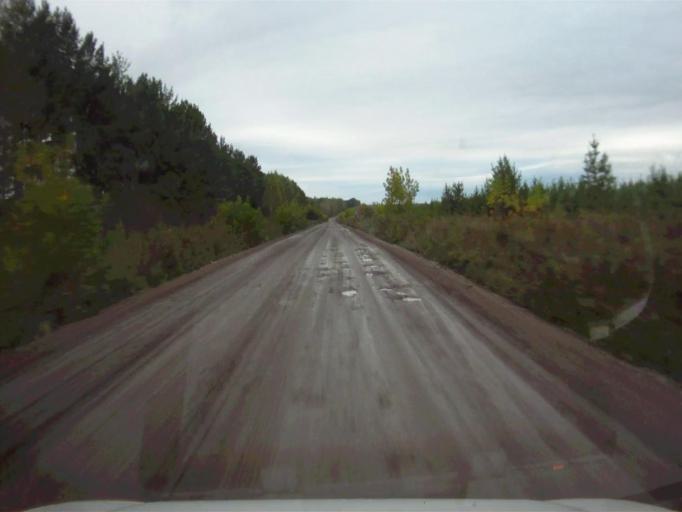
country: RU
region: Sverdlovsk
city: Mikhaylovsk
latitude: 56.1466
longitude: 59.2793
